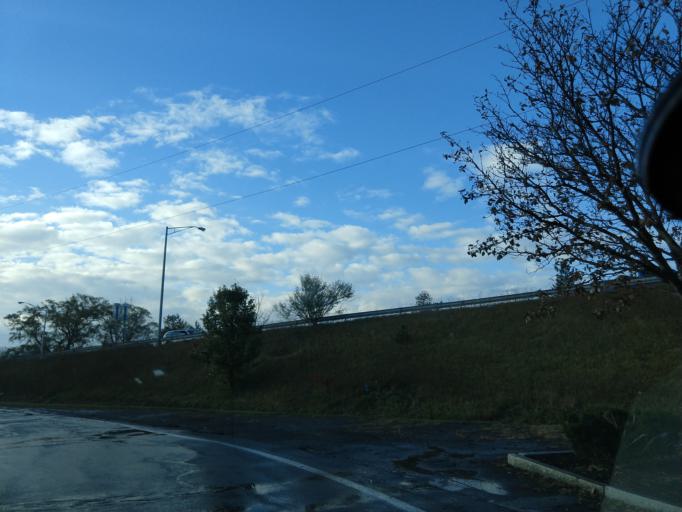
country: US
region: New York
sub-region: Tompkins County
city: Lansing
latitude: 42.4804
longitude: -76.4828
